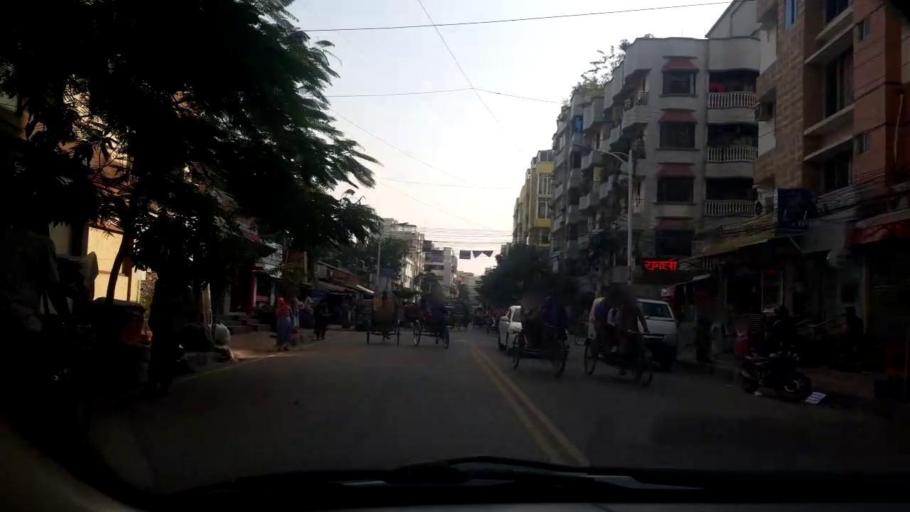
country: BD
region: Dhaka
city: Tungi
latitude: 23.8662
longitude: 90.3887
